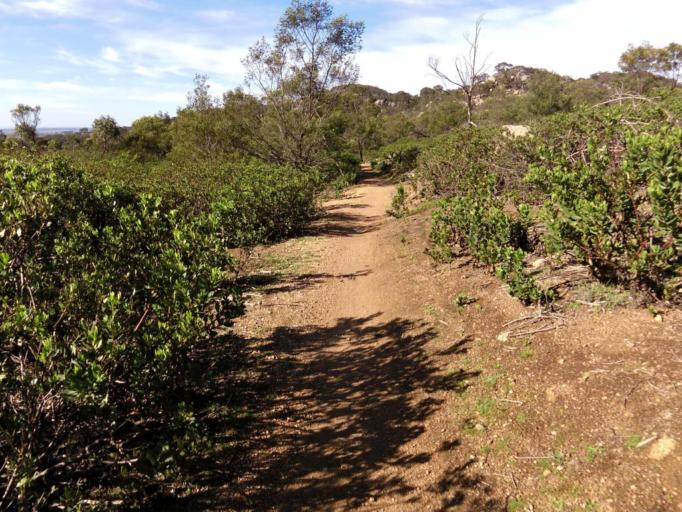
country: AU
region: Victoria
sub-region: Wyndham
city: Little River
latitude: -37.9290
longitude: 144.4359
